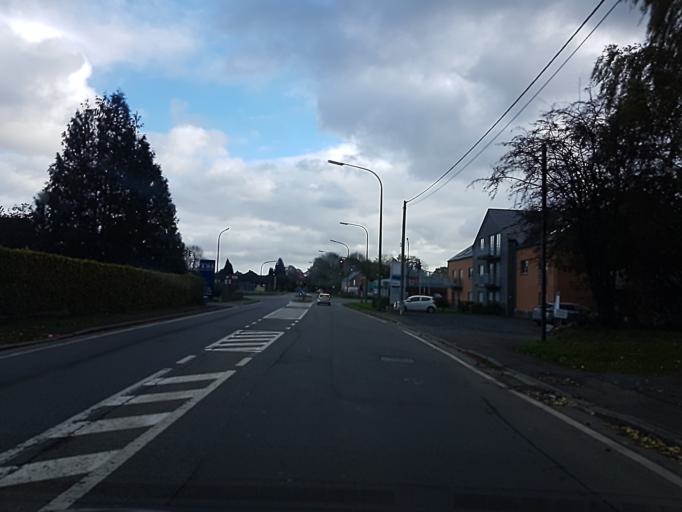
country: BE
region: Wallonia
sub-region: Province de Liege
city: Trooz
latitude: 50.5251
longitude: 5.7230
